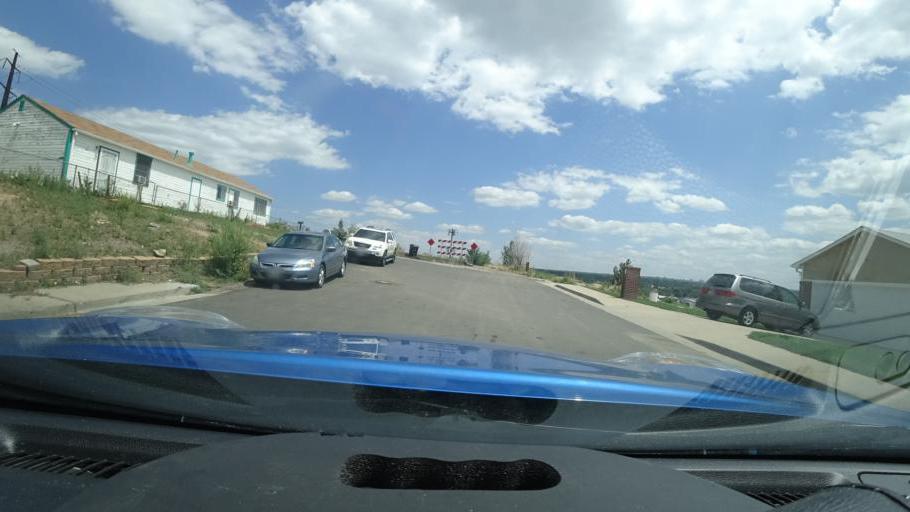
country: US
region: Colorado
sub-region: Arapahoe County
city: Englewood
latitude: 39.6805
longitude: -105.0069
